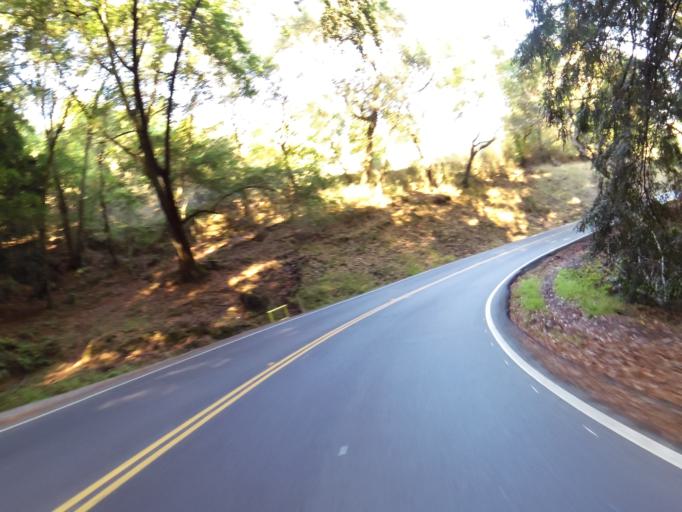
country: US
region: California
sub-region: Marin County
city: Corte Madera
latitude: 37.9197
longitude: -122.5303
